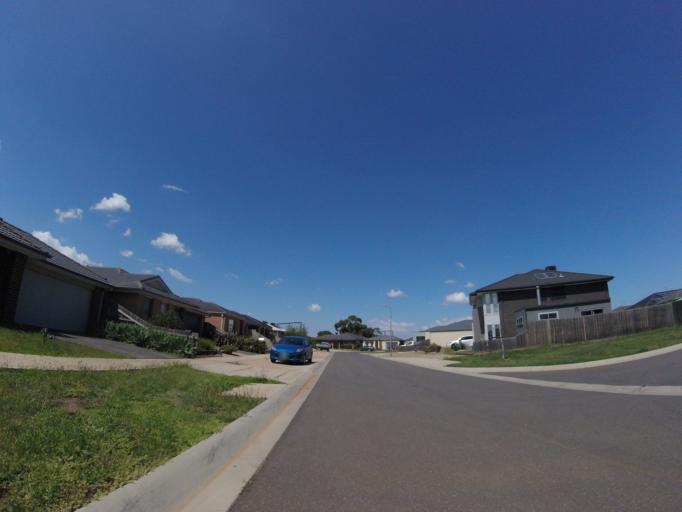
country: AU
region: Victoria
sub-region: Hume
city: Diggers Rest
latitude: -37.6235
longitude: 144.7179
